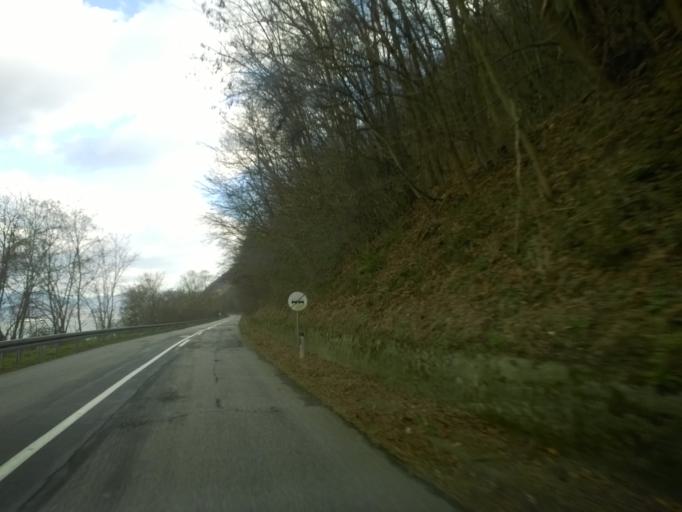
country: RO
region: Caras-Severin
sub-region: Comuna Berzasca
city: Liubcova
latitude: 44.6462
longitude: 21.8696
